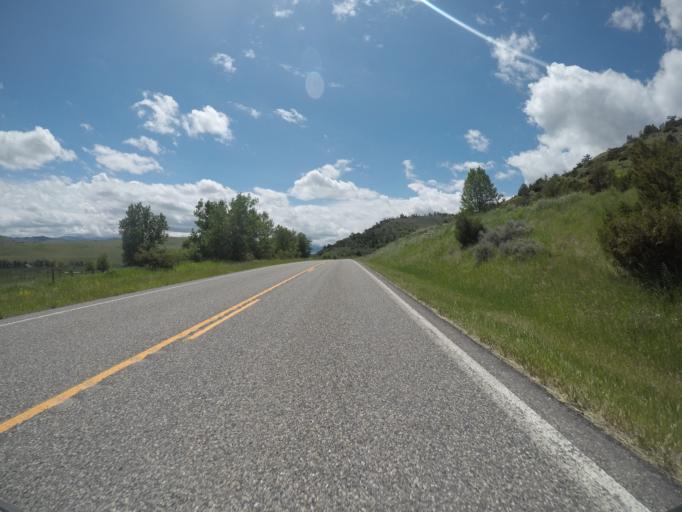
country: US
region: Montana
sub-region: Sweet Grass County
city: Big Timber
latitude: 45.6794
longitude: -110.0873
